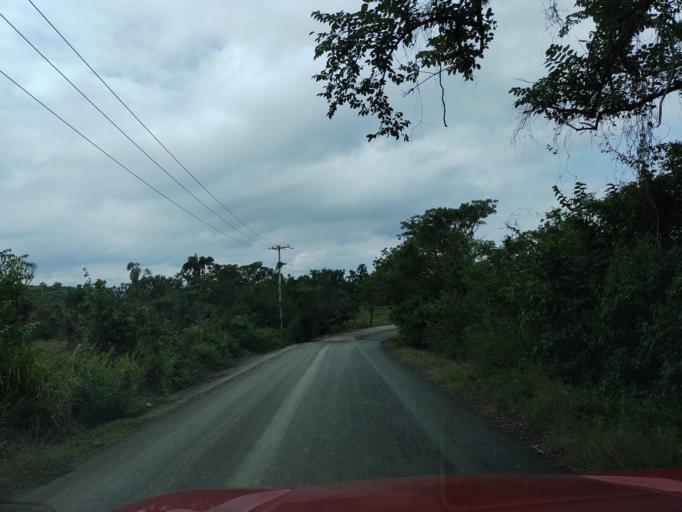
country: MX
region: Veracruz
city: Coatzintla
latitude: 20.4570
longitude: -97.4466
